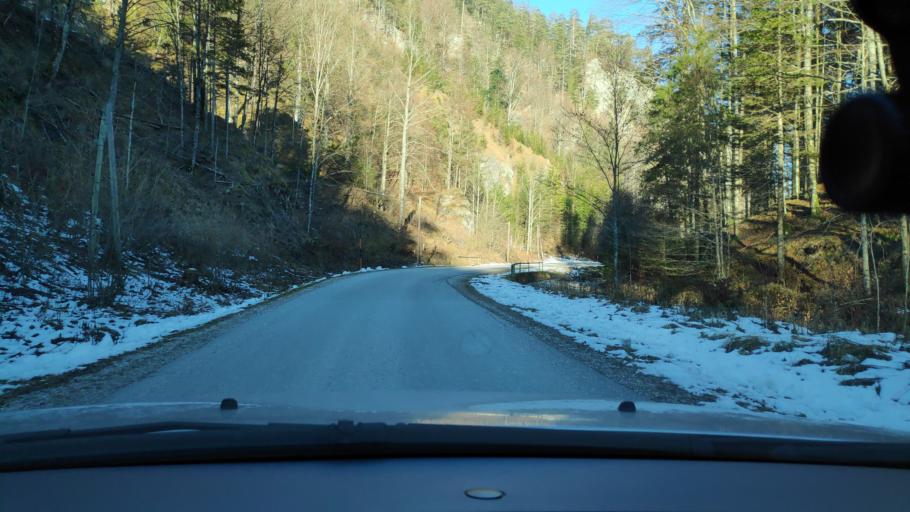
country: AT
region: Lower Austria
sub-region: Politischer Bezirk Neunkirchen
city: Schwarzau im Gebirge
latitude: 47.7519
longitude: 15.6799
